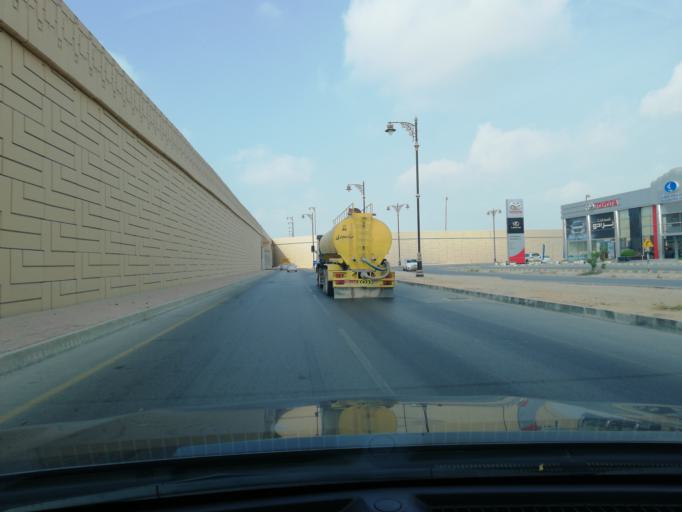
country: OM
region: Zufar
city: Salalah
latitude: 17.0185
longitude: 54.0605
